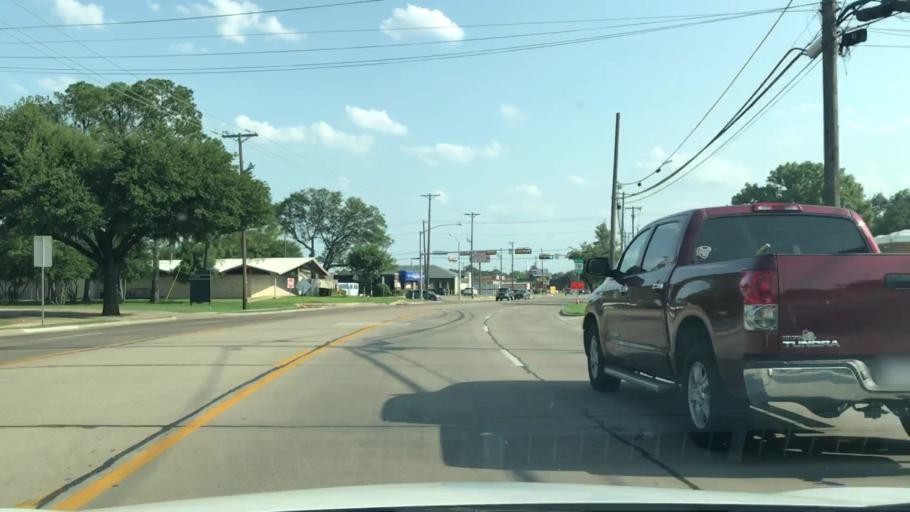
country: US
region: Texas
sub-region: Dallas County
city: Irving
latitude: 32.8222
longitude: -96.9497
